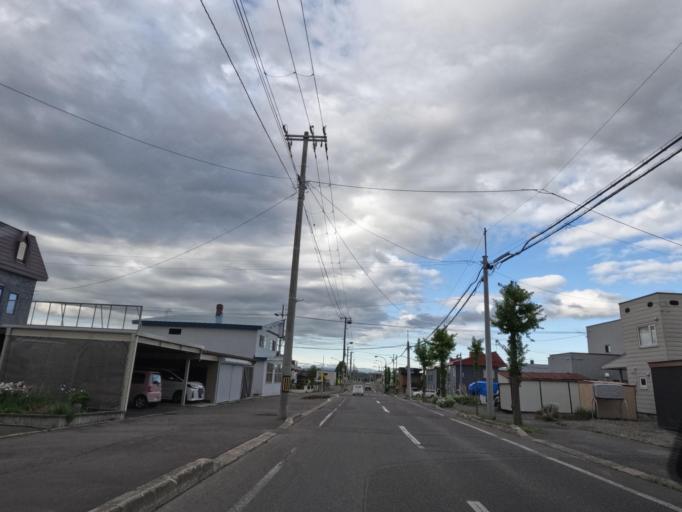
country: JP
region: Hokkaido
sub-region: Asahikawa-shi
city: Asahikawa
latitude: 43.7737
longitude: 142.3133
